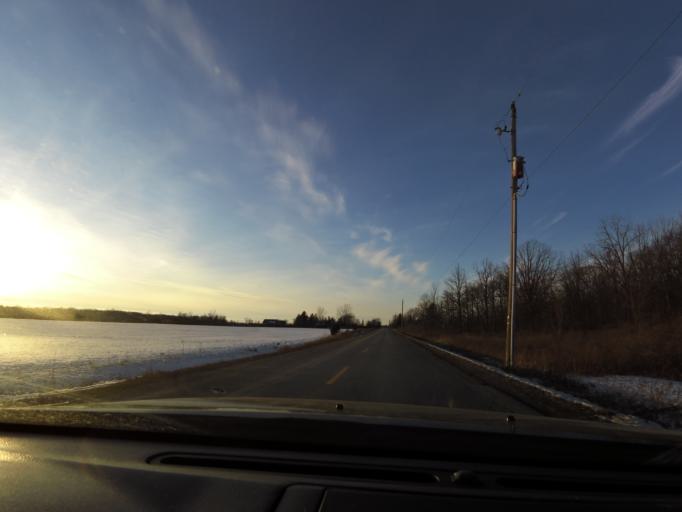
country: CA
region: Ontario
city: Hamilton
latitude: 43.1084
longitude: -79.6330
